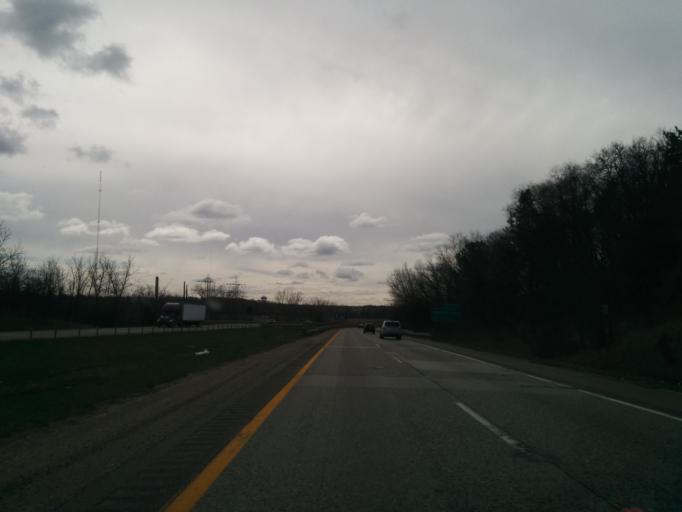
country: US
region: Michigan
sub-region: Kent County
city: Grand Rapids
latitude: 42.9586
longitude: -85.7071
